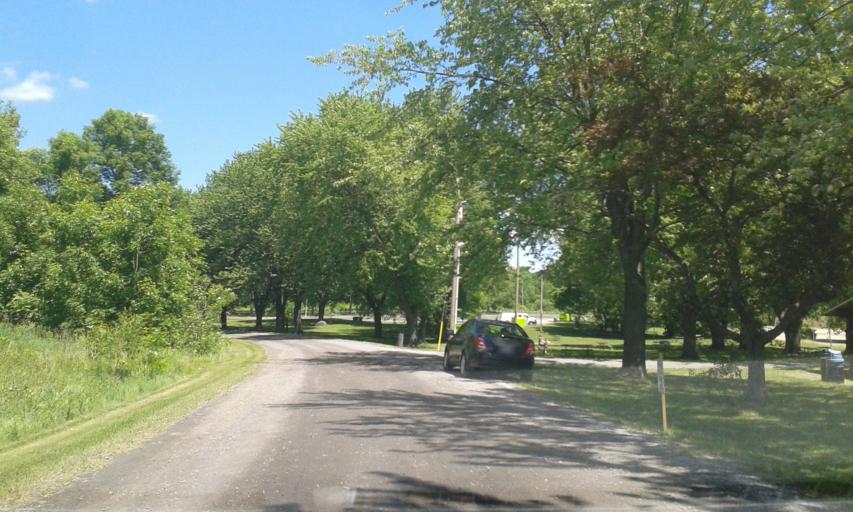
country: US
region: New York
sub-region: St. Lawrence County
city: Massena
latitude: 45.0156
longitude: -74.8924
